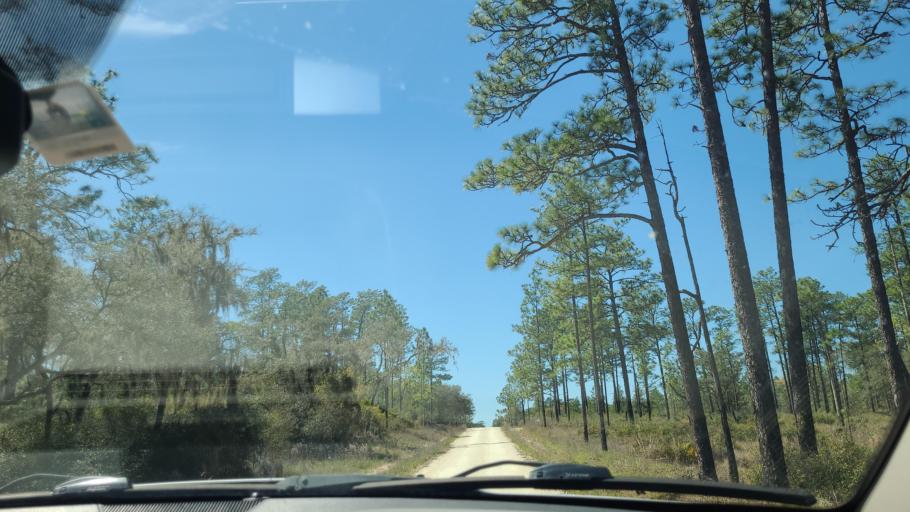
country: US
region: Florida
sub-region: Putnam County
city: Interlachen
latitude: 29.4288
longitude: -81.8133
